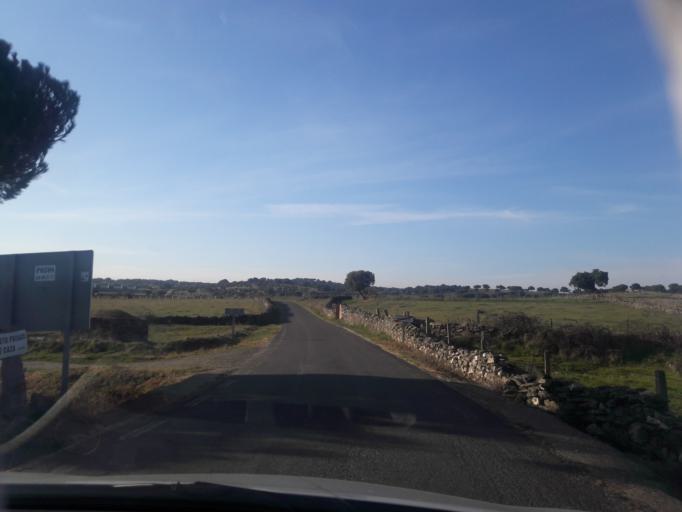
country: ES
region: Castille and Leon
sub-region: Provincia de Salamanca
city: Montejo
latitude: 40.6301
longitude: -5.6205
